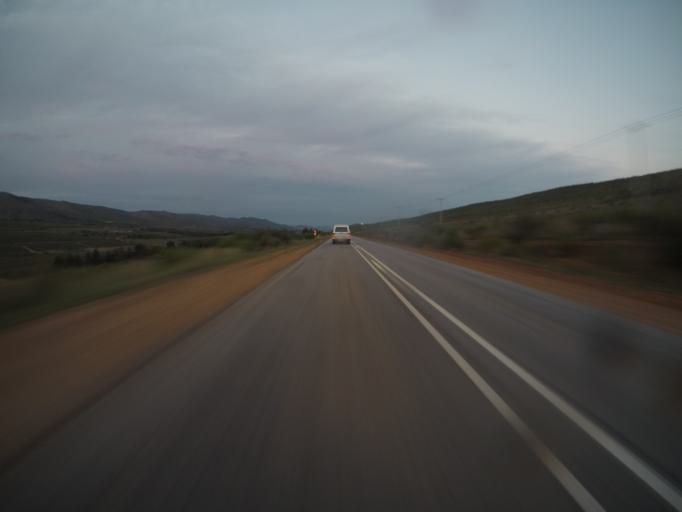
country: ZA
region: Western Cape
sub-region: Eden District Municipality
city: Plettenberg Bay
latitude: -33.8094
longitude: 23.7029
